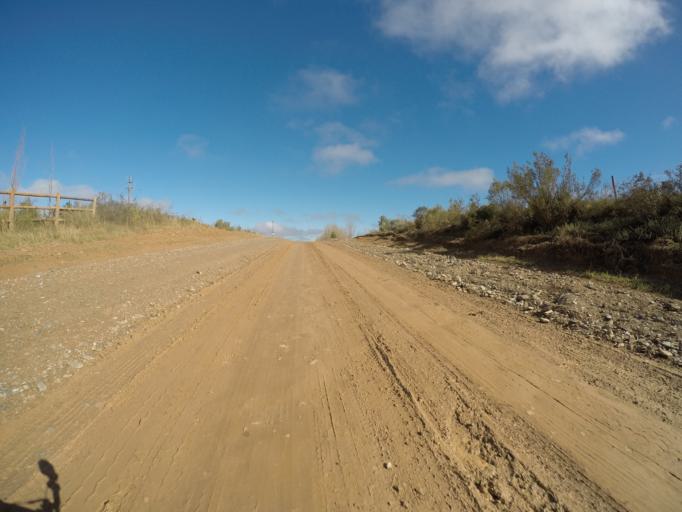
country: ZA
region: Western Cape
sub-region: Overberg District Municipality
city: Caledon
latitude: -34.1136
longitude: 19.7439
